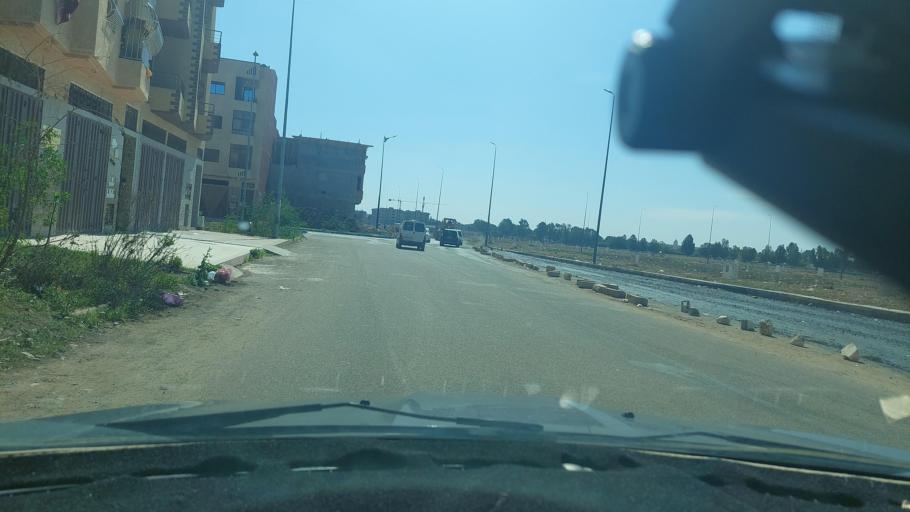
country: MA
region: Grand Casablanca
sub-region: Mediouna
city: Mediouna
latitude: 33.3817
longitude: -7.5368
